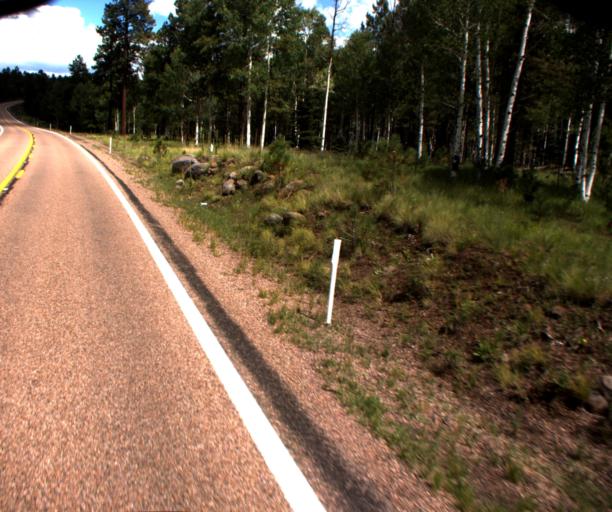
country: US
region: Arizona
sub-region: Navajo County
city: Pinetop-Lakeside
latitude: 34.0254
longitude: -109.6374
